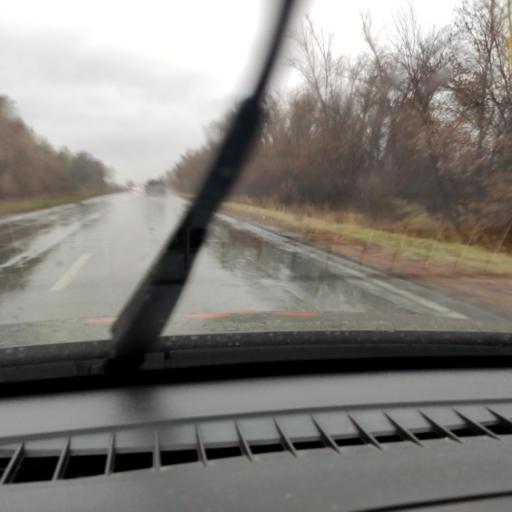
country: RU
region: Samara
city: Tol'yatti
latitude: 53.6273
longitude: 49.3053
